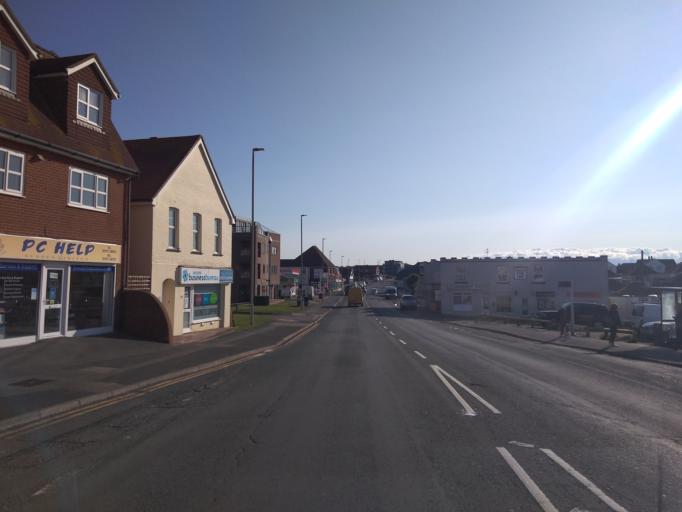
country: GB
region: England
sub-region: East Sussex
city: Peacehaven
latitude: 50.7910
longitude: 0.0014
